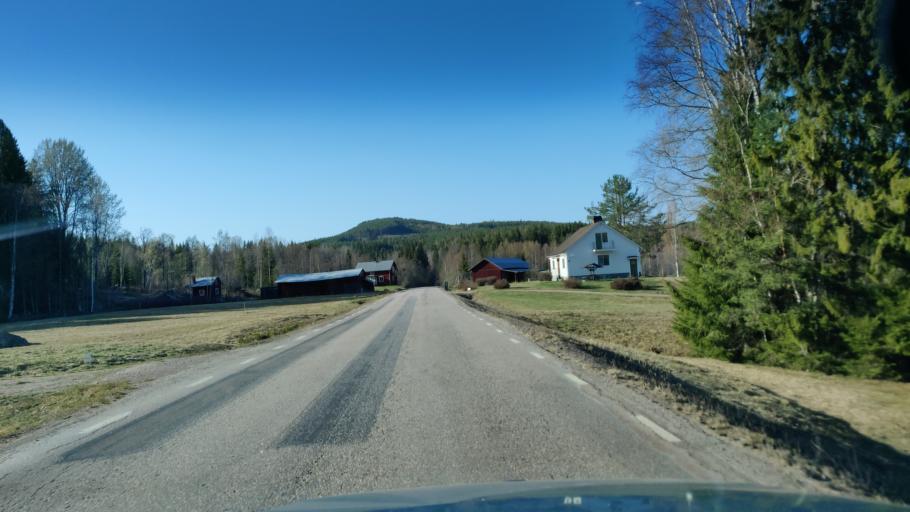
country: SE
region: Vaermland
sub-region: Munkfors Kommun
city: Munkfors
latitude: 59.9744
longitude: 13.4144
